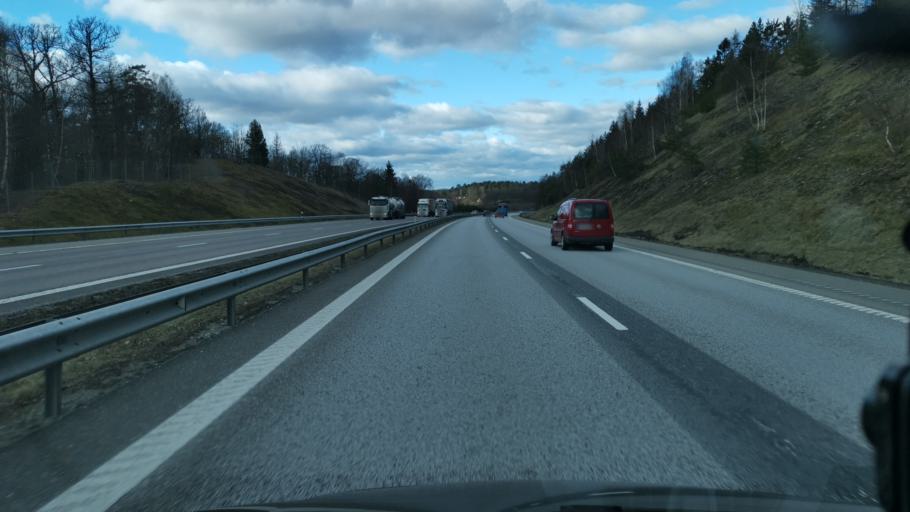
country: SE
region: Vaestra Goetaland
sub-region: Uddevalla Kommun
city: Ljungskile
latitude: 58.1959
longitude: 11.9078
